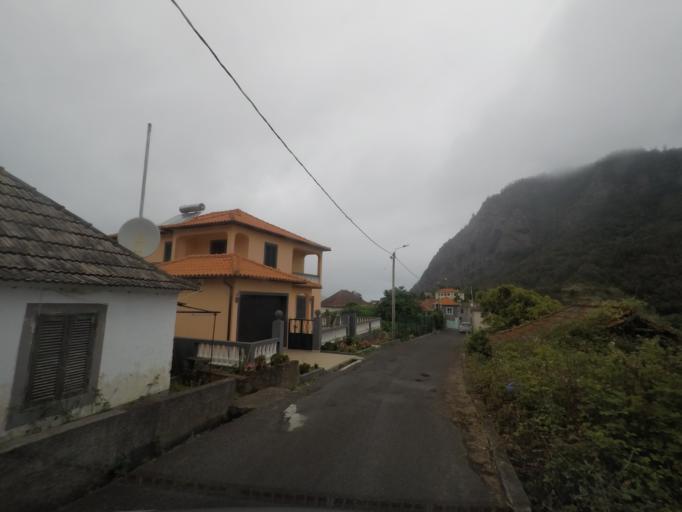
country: PT
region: Madeira
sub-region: Santana
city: Santana
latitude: 32.7700
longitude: -16.8438
